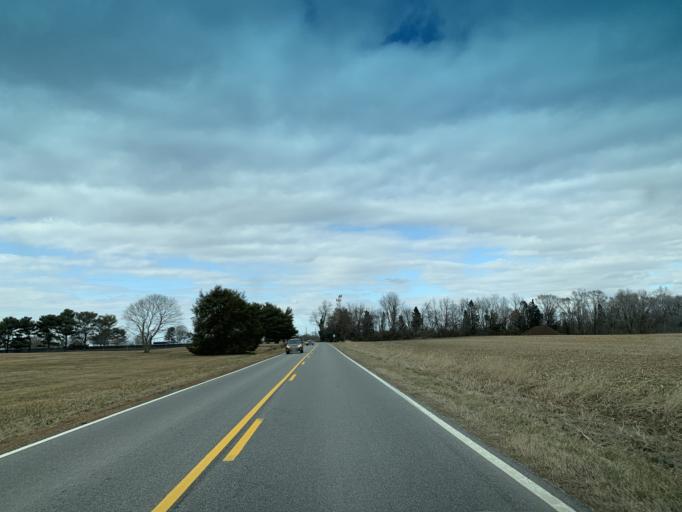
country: US
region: Maryland
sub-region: Queen Anne's County
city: Centreville
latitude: 38.9476
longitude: -76.0793
